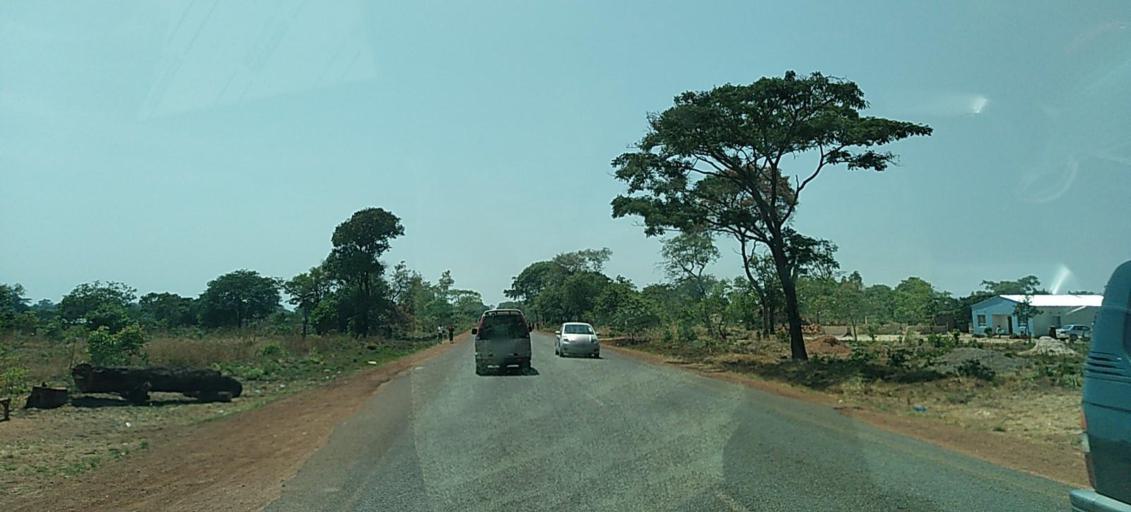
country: ZM
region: North-Western
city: Solwezi
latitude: -12.3178
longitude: 25.8638
